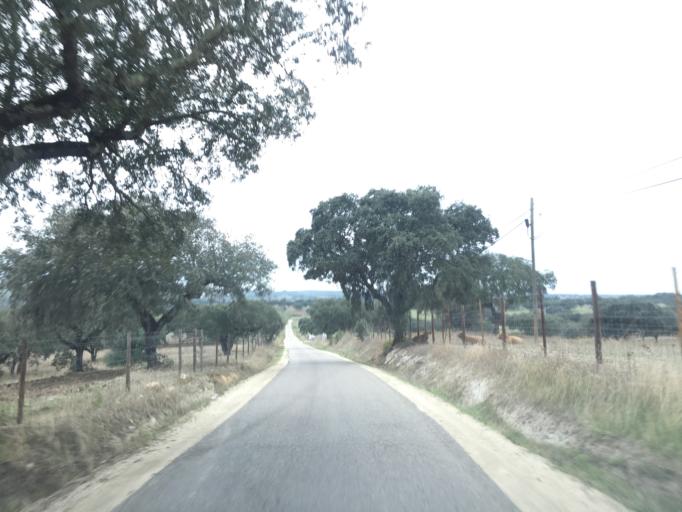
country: PT
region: Portalegre
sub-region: Fronteira
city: Vale da Amoreira
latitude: 39.0512
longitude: -7.7738
